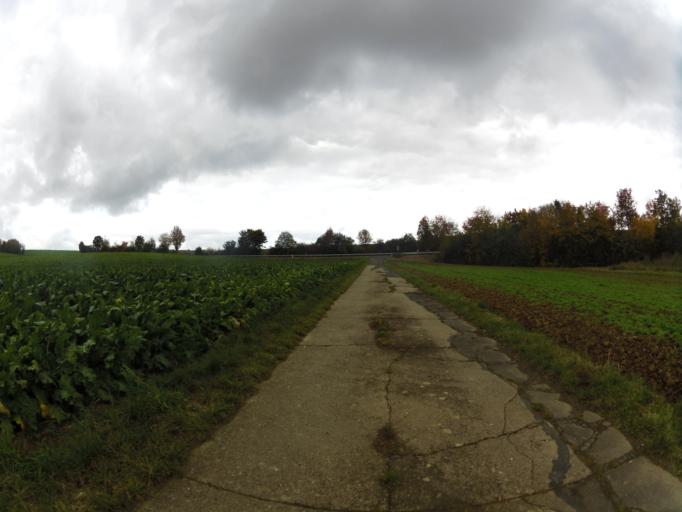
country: DE
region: Bavaria
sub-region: Regierungsbezirk Unterfranken
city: Kurnach
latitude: 49.8730
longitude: 10.0094
